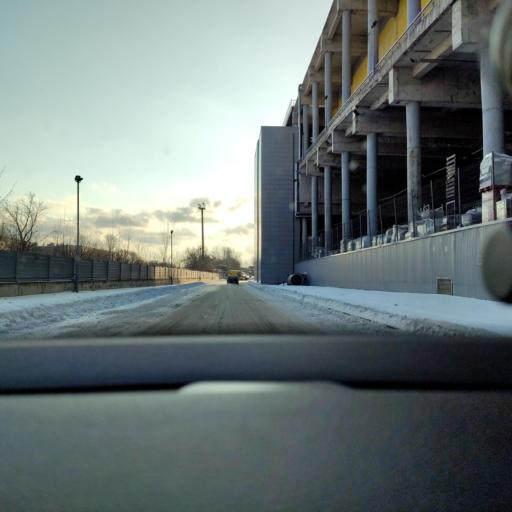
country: RU
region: Moscow
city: Lefortovo
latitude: 55.7482
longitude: 37.7087
